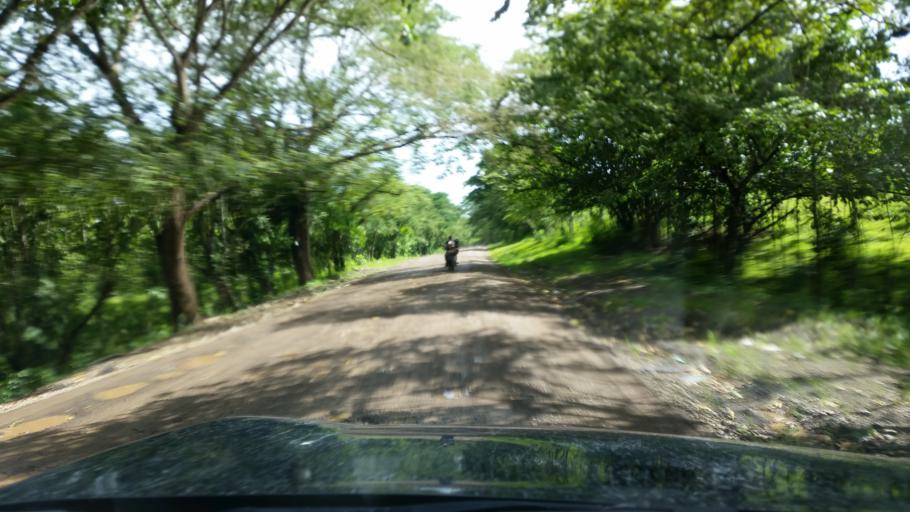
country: NI
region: Atlantico Norte (RAAN)
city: Siuna
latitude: 13.7040
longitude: -84.7787
